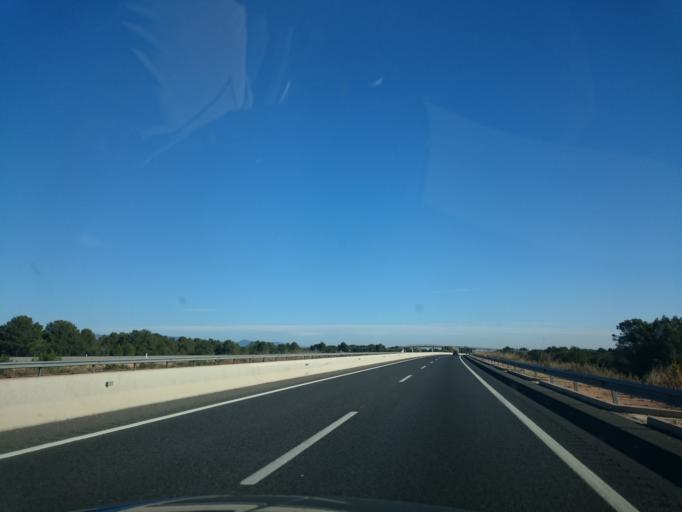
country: ES
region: Catalonia
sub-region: Provincia de Tarragona
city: Vilanova d'Escornalbou
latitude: 41.0454
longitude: 0.9690
